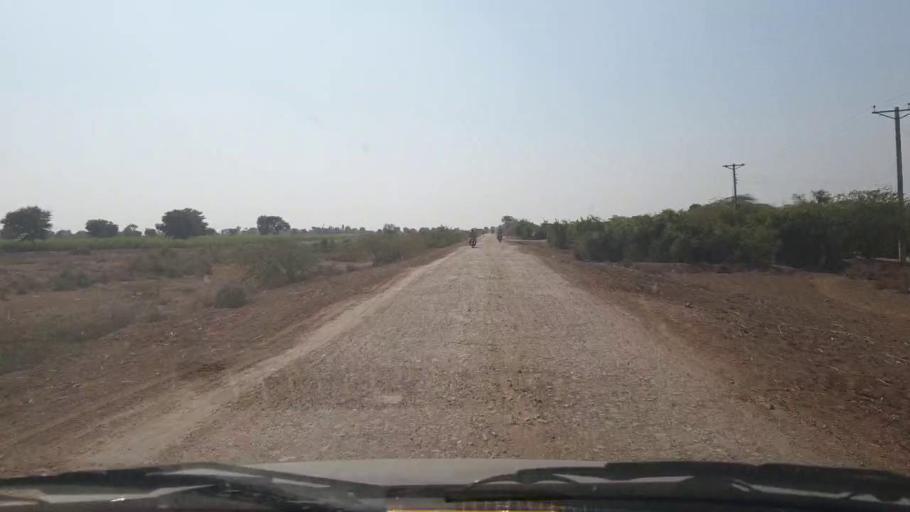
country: PK
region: Sindh
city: Samaro
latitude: 25.2271
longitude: 69.3346
